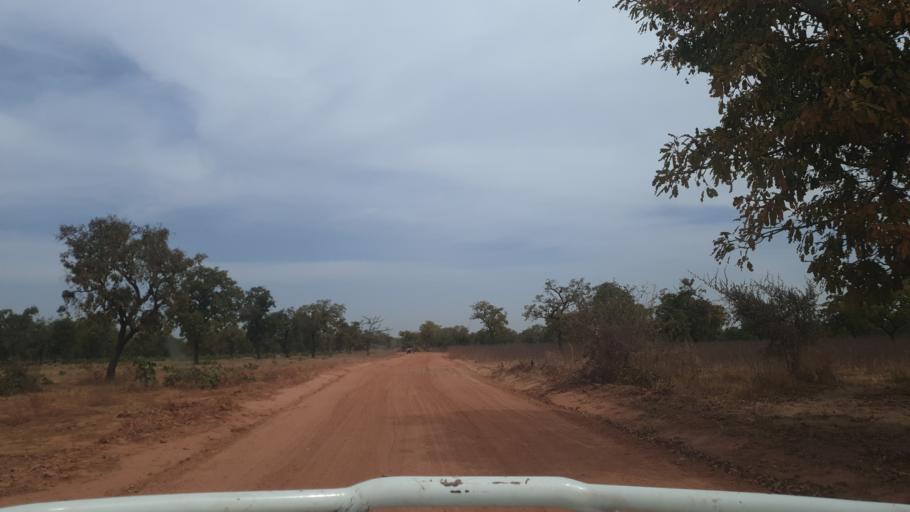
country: ML
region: Sikasso
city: Yorosso
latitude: 12.2225
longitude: -4.7532
